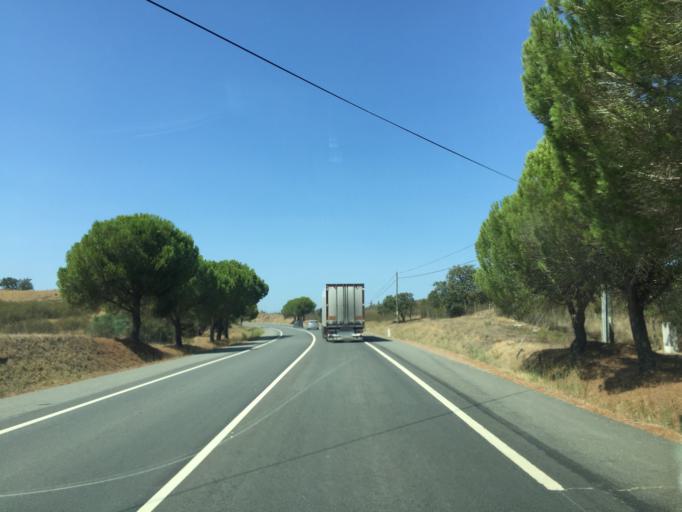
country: PT
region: Faro
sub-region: Silves
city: Sao Bartolomeu de Messines
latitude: 37.2876
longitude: -8.2946
